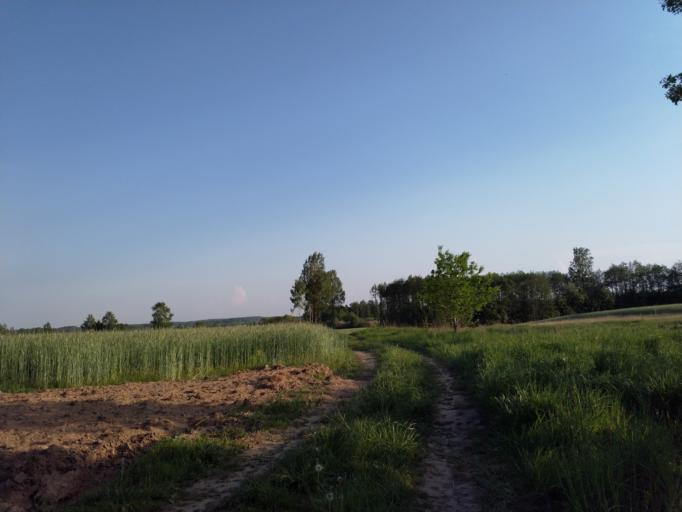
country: LV
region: Aizpute
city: Aizpute
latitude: 56.8310
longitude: 21.7824
